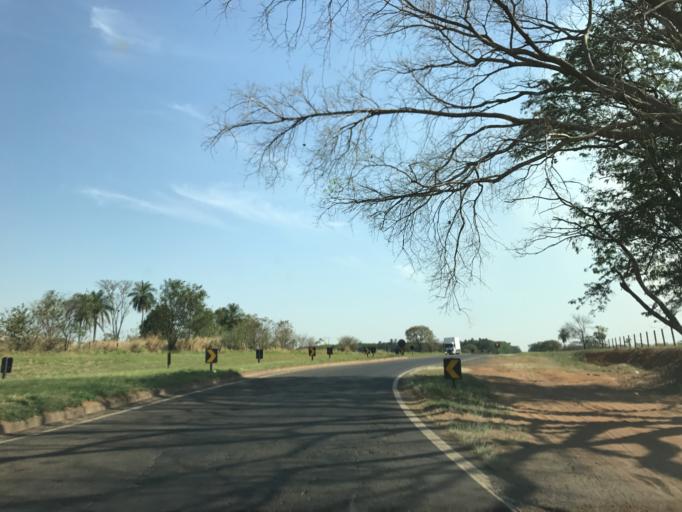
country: BR
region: Sao Paulo
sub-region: Penapolis
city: Penapolis
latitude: -21.3865
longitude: -50.0965
